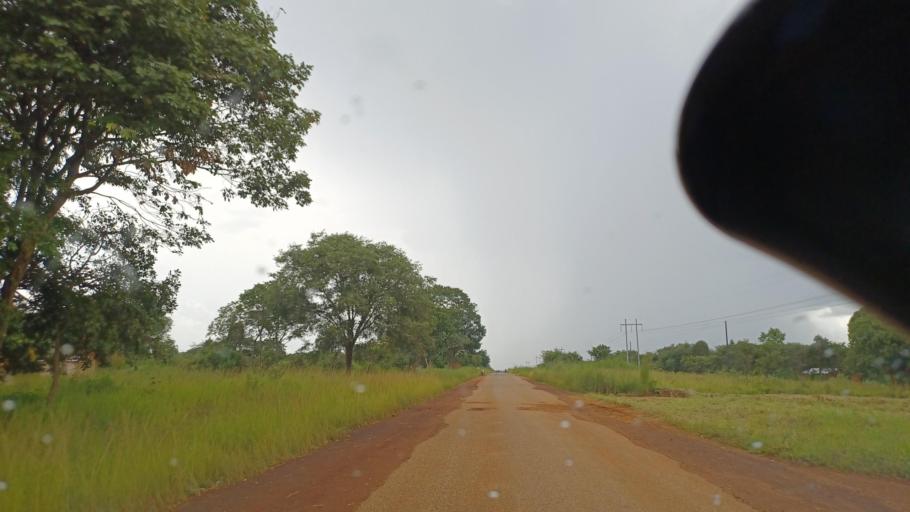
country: ZM
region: North-Western
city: Kasempa
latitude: -13.0507
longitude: 25.9890
